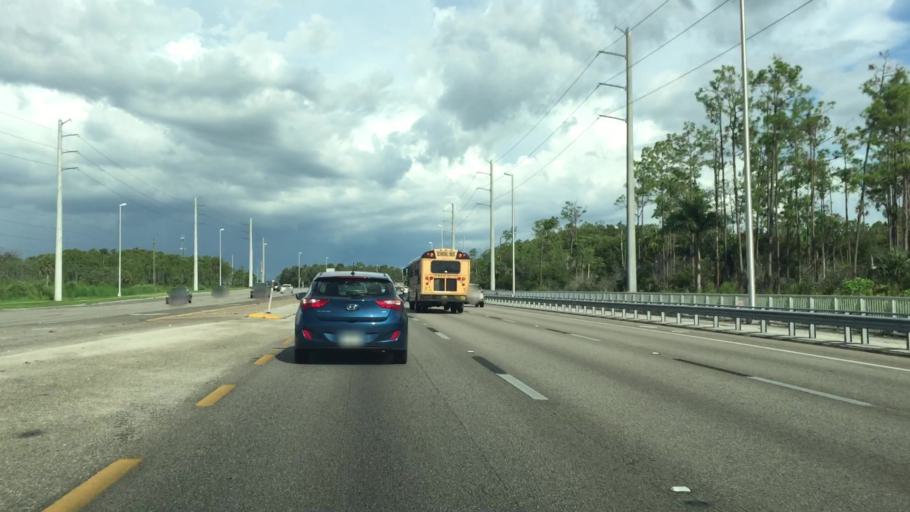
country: US
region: Florida
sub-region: Lee County
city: Tice
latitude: 26.6304
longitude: -81.7809
